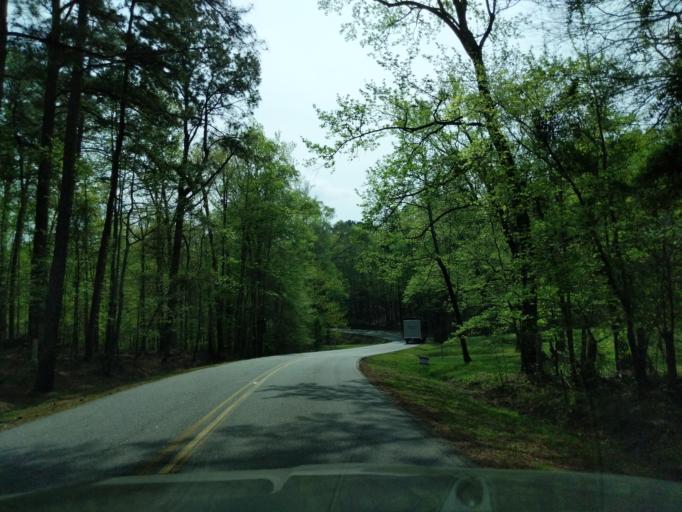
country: US
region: Georgia
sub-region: Lincoln County
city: Lincolnton
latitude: 33.8510
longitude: -82.4019
